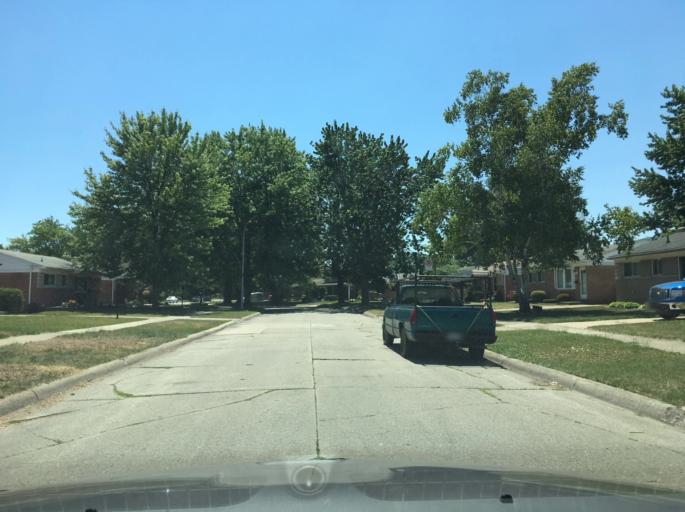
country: US
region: Michigan
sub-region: Macomb County
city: Fraser
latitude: 42.5417
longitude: -82.9242
